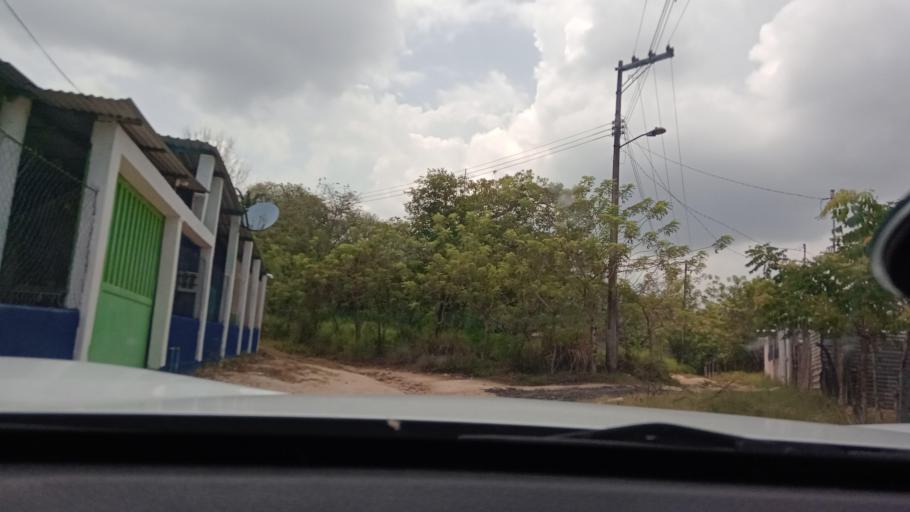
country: MX
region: Veracruz
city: Las Choapas
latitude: 17.8873
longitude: -94.1031
